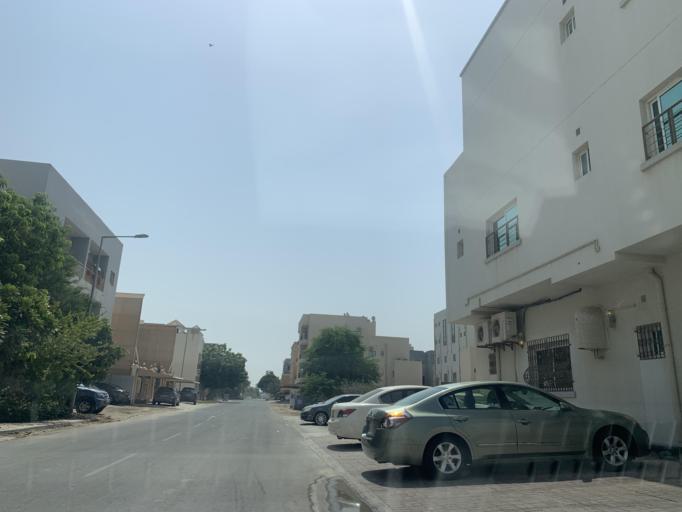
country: BH
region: Manama
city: Jidd Hafs
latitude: 26.2075
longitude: 50.5037
